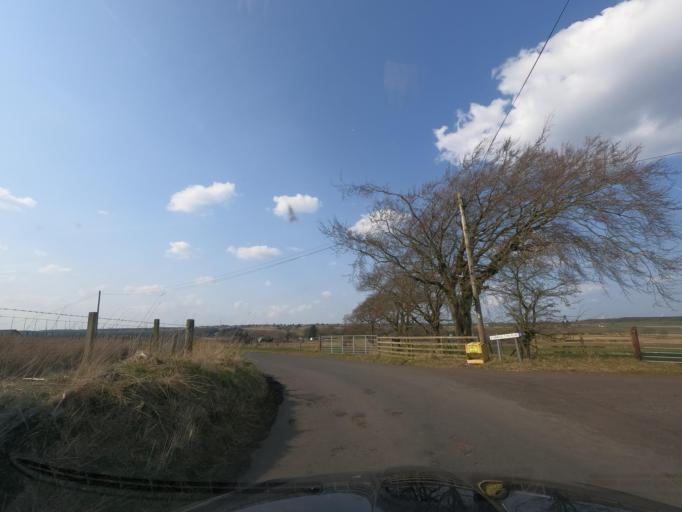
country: GB
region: Scotland
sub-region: South Lanarkshire
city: Forth
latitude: 55.7584
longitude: -3.6624
